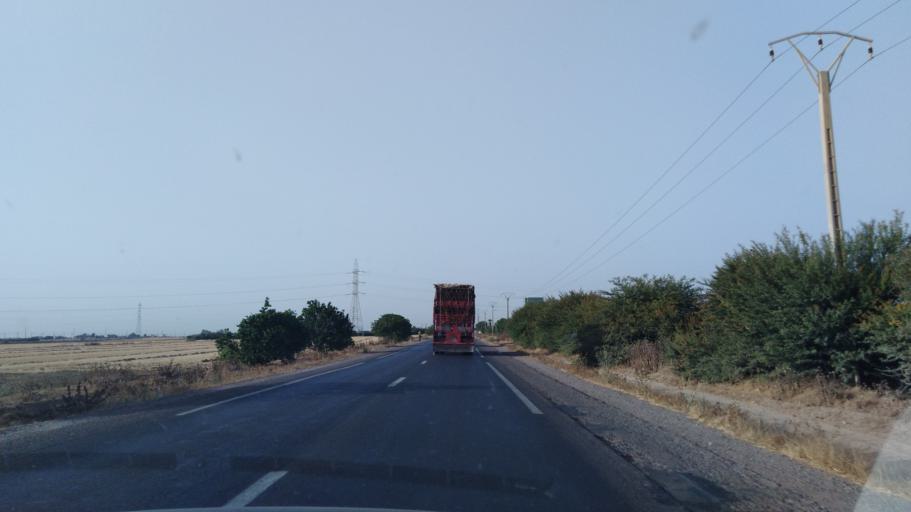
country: MA
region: Chaouia-Ouardigha
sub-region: Settat Province
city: Berrechid
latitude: 33.1424
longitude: -7.6230
